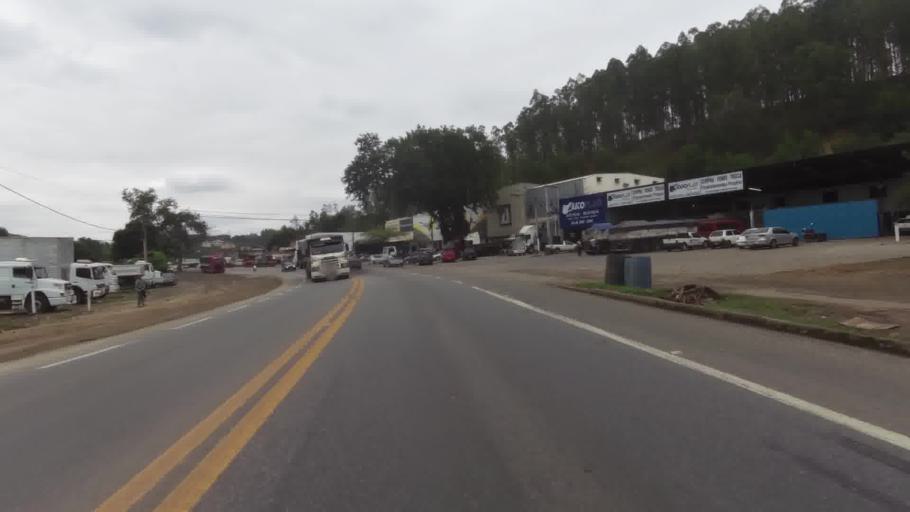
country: BR
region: Espirito Santo
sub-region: Iconha
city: Iconha
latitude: -20.7899
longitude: -40.8031
